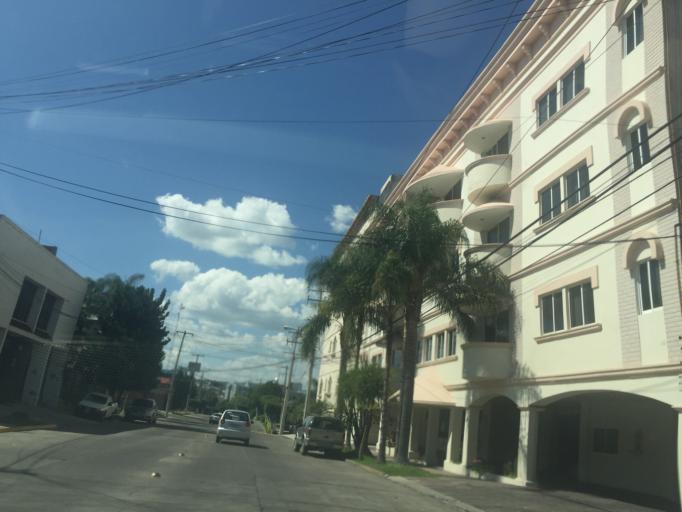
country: MX
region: Guanajuato
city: Leon
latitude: 21.1487
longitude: -101.6948
